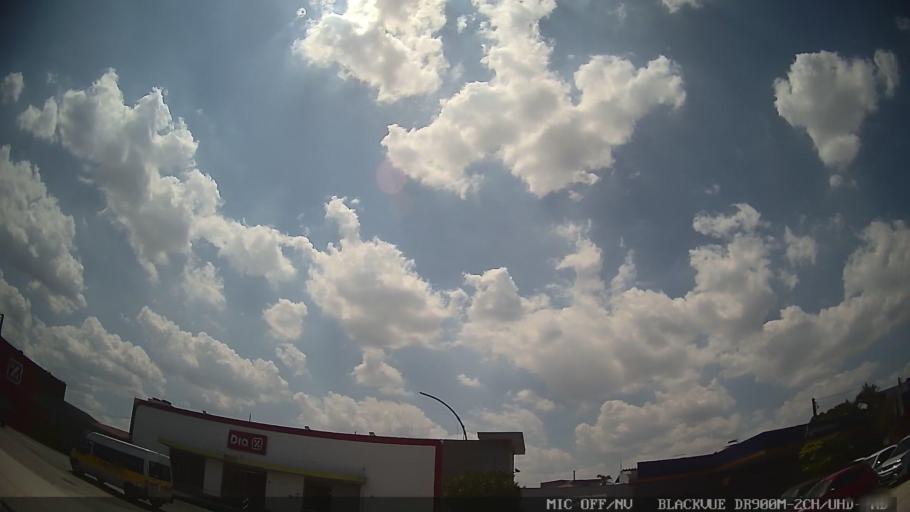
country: BR
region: Sao Paulo
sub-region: Taboao Da Serra
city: Taboao da Serra
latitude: -23.6805
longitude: -46.7960
